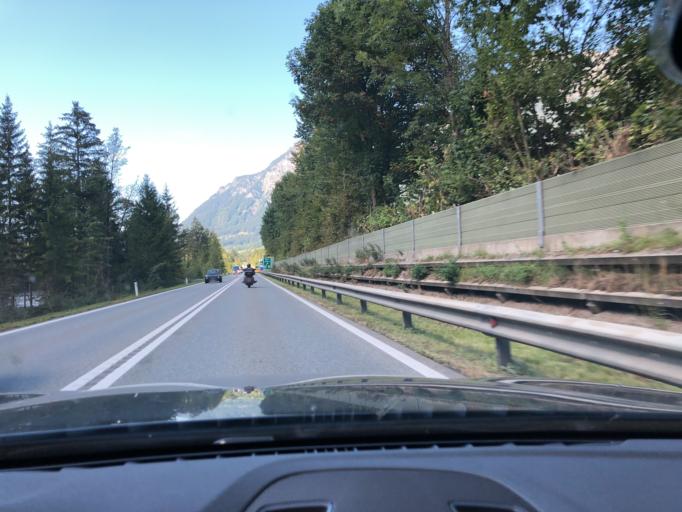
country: AT
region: Vorarlberg
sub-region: Politischer Bezirk Bludenz
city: Innerbraz
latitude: 47.1391
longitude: 9.9291
